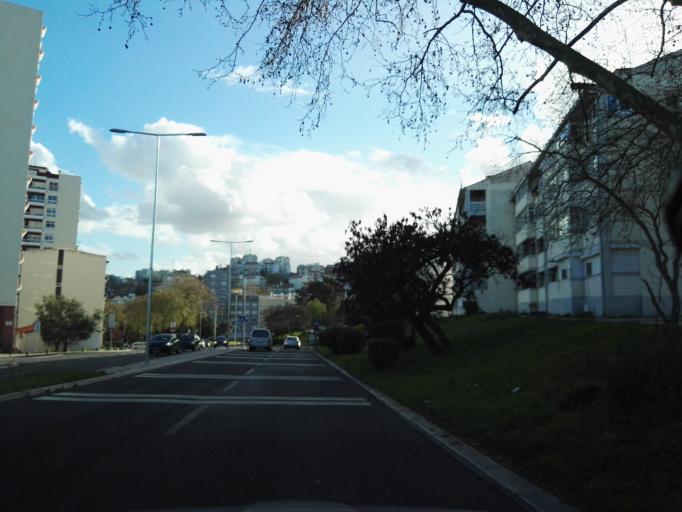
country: PT
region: Lisbon
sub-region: Loures
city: Moscavide
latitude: 38.7700
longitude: -9.1093
